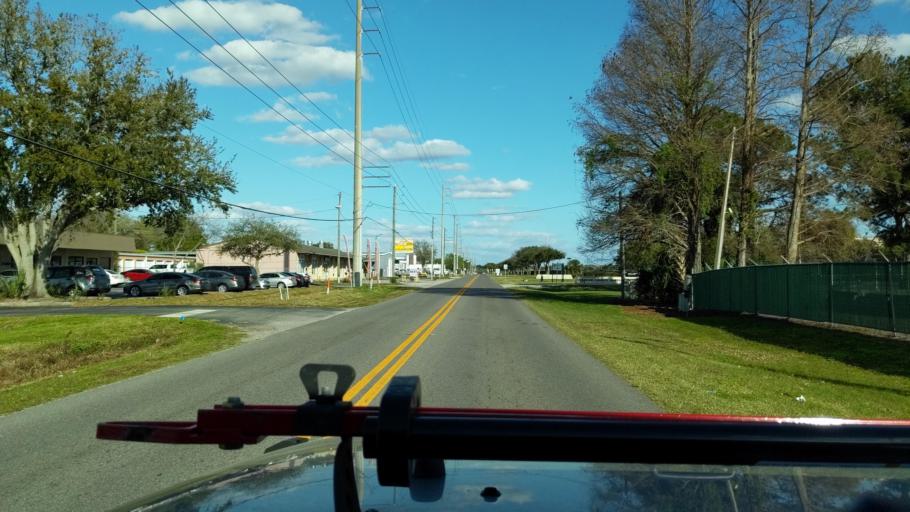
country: US
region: Florida
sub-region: Orange County
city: Ocoee
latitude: 28.5588
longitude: -81.5559
